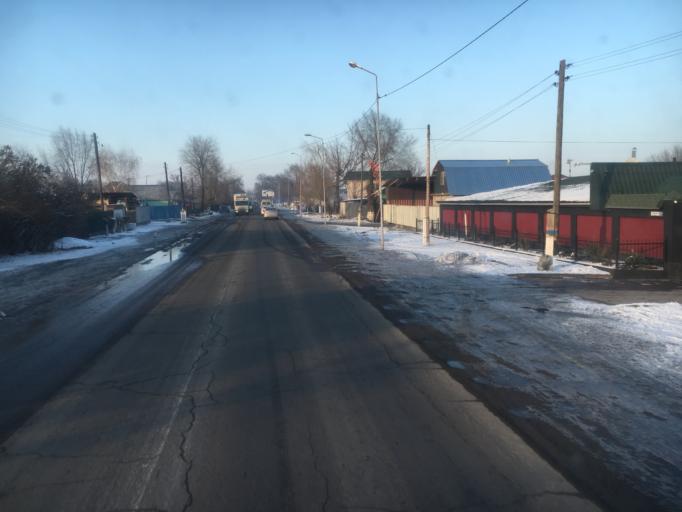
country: KZ
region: Almaty Oblysy
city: Burunday
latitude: 43.3723
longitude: 76.6417
